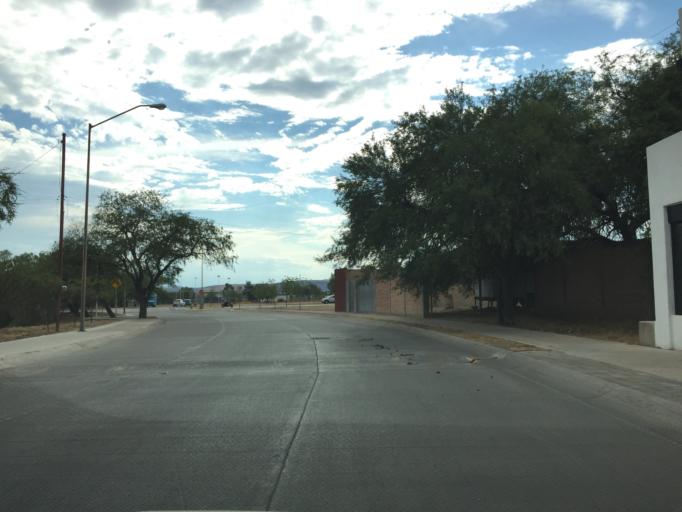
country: MX
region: Aguascalientes
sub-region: Jesus Maria
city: El Llano
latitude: 21.9305
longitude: -102.3043
